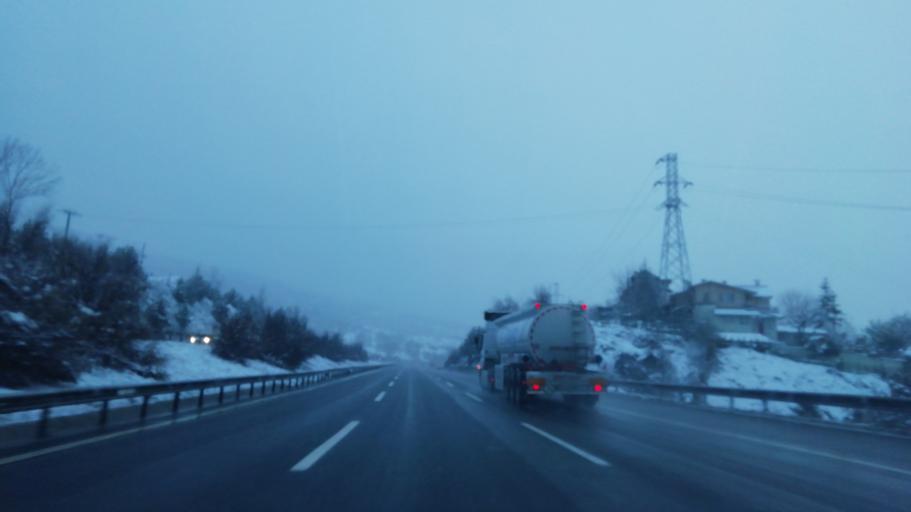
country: TR
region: Bolu
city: Bolu
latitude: 40.7582
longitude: 31.5831
